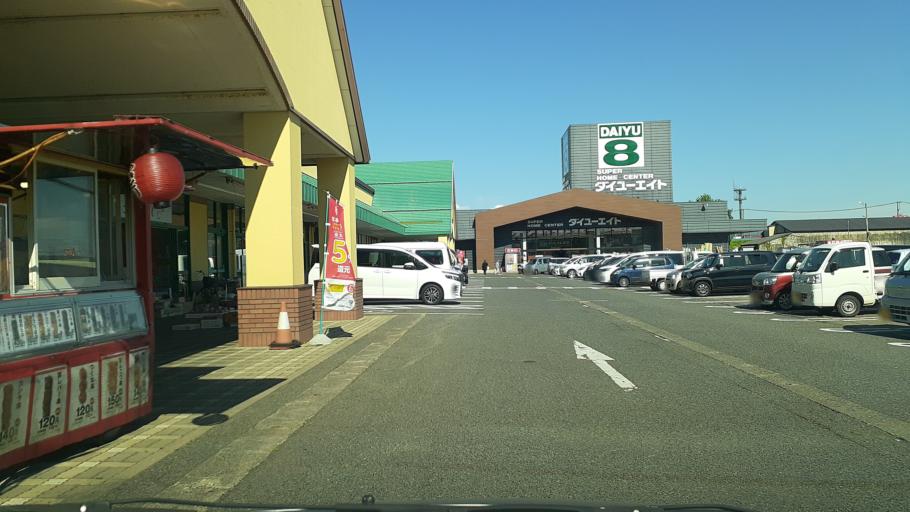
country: JP
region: Fukushima
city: Kitakata
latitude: 37.5662
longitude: 139.8164
